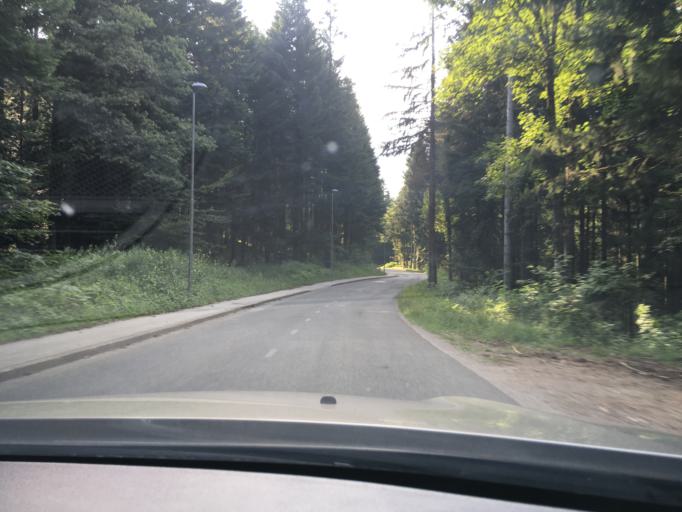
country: SI
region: Dolenjske Toplice
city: Dolenjske Toplice
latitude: 45.7606
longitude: 15.0483
